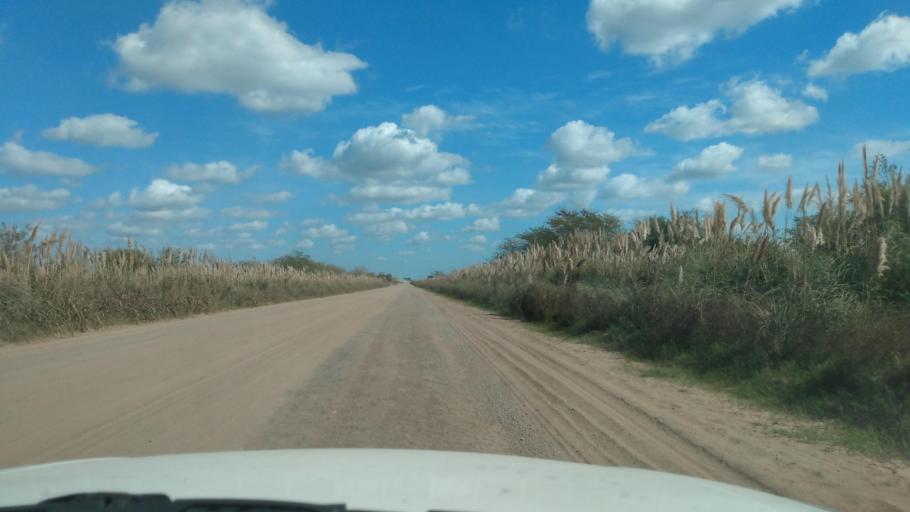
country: AR
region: Buenos Aires
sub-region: Partido de Navarro
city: Navarro
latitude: -35.0014
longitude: -59.3508
